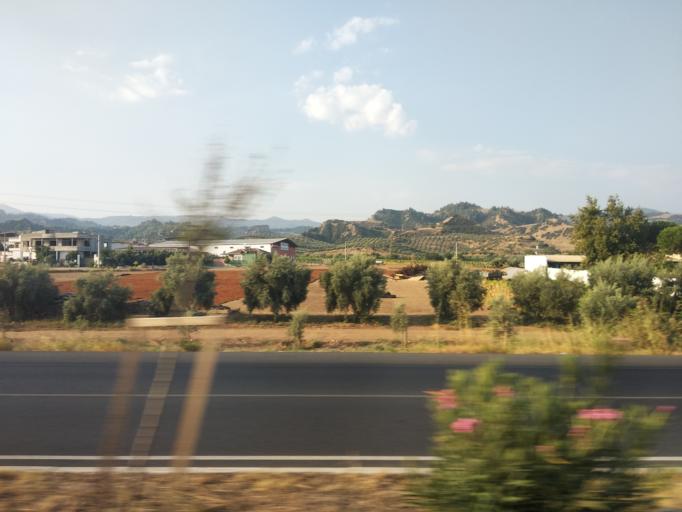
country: TR
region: Manisa
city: Ahmetli
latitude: 38.5064
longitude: 27.9965
